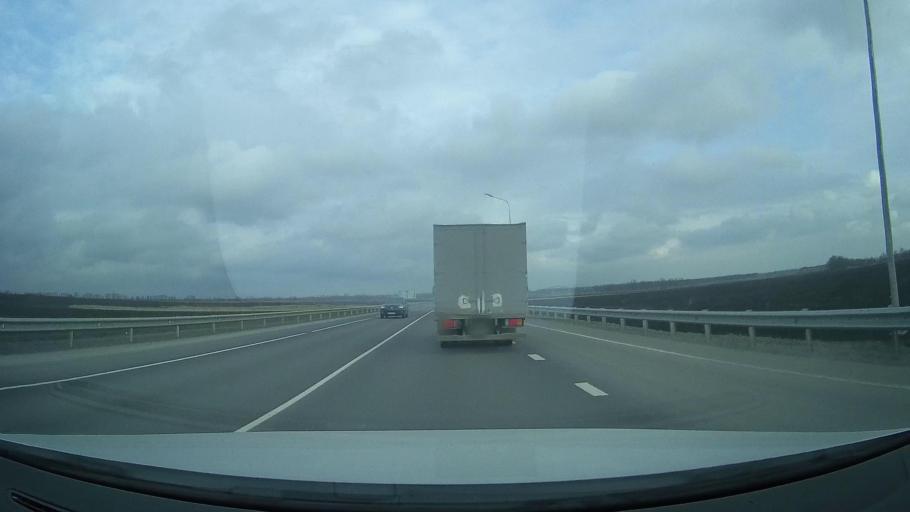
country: RU
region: Rostov
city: Grushevskaya
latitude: 47.4588
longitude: 39.8867
